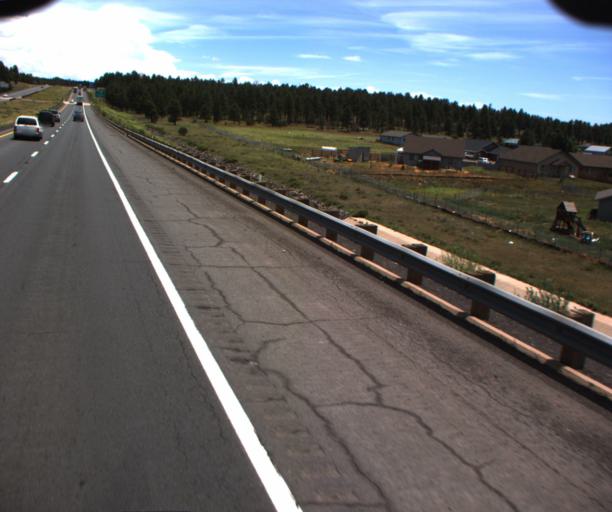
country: US
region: Arizona
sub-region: Coconino County
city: Williams
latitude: 35.2638
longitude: -112.1766
